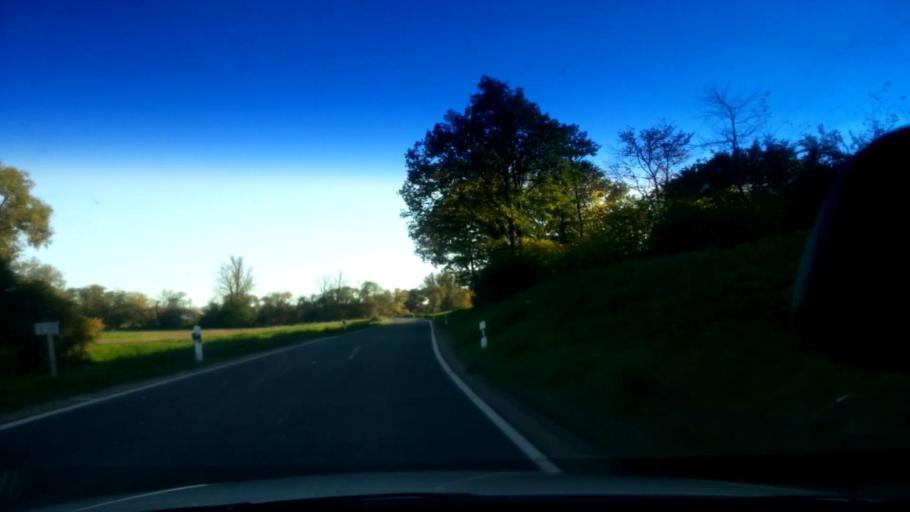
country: DE
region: Bavaria
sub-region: Upper Franconia
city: Rattelsdorf
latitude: 50.0112
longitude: 10.8732
